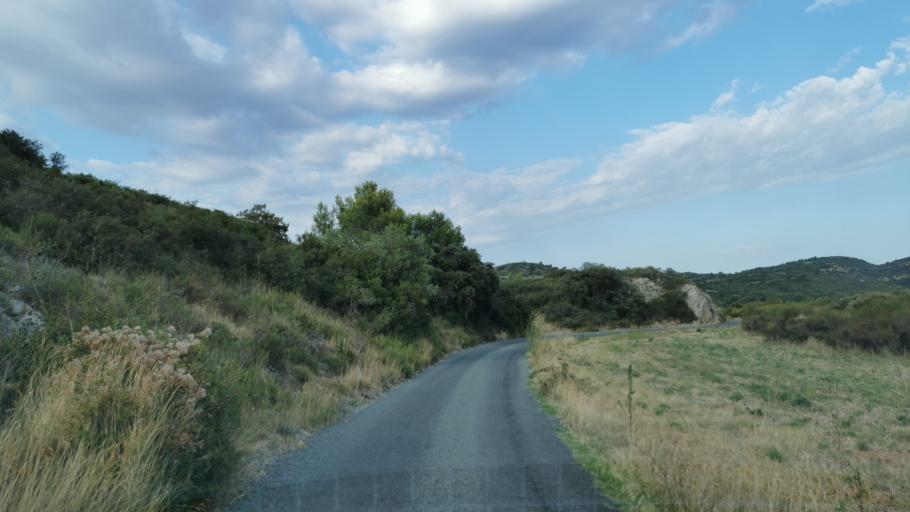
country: FR
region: Languedoc-Roussillon
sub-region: Departement de l'Aude
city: Nevian
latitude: 43.1910
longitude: 2.8924
